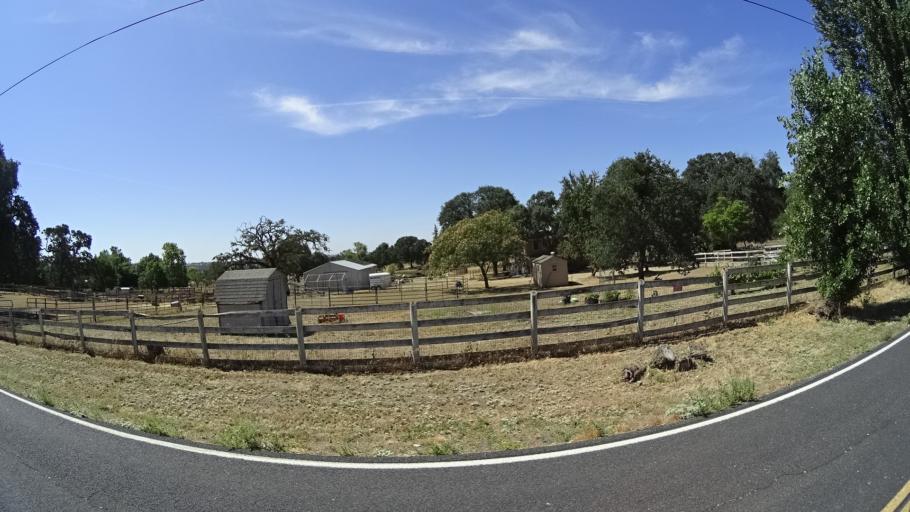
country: US
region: California
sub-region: Calaveras County
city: Rancho Calaveras
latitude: 38.1484
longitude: -120.9340
